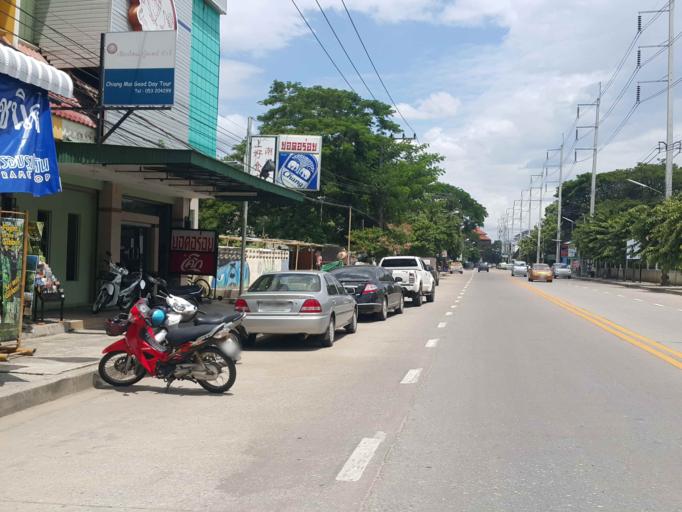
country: TH
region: Chiang Mai
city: Chiang Mai
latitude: 18.7659
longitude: 99.0002
